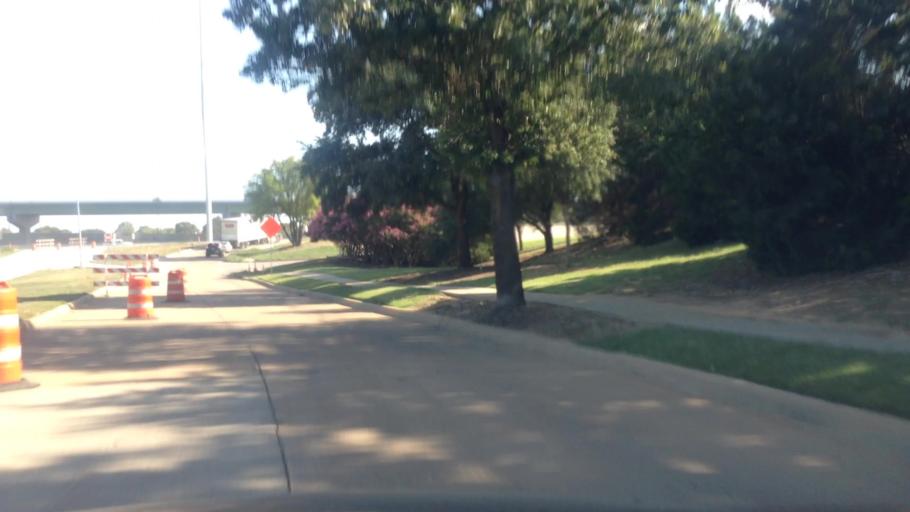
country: US
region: Texas
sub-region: Dallas County
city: Irving
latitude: 32.8391
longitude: -96.9206
